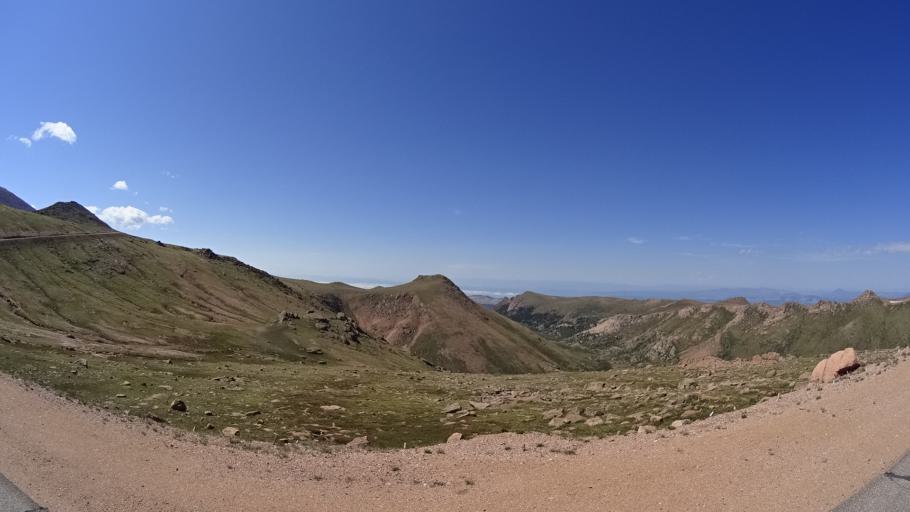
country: US
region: Colorado
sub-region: El Paso County
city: Cascade-Chipita Park
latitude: 38.8580
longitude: -105.0658
